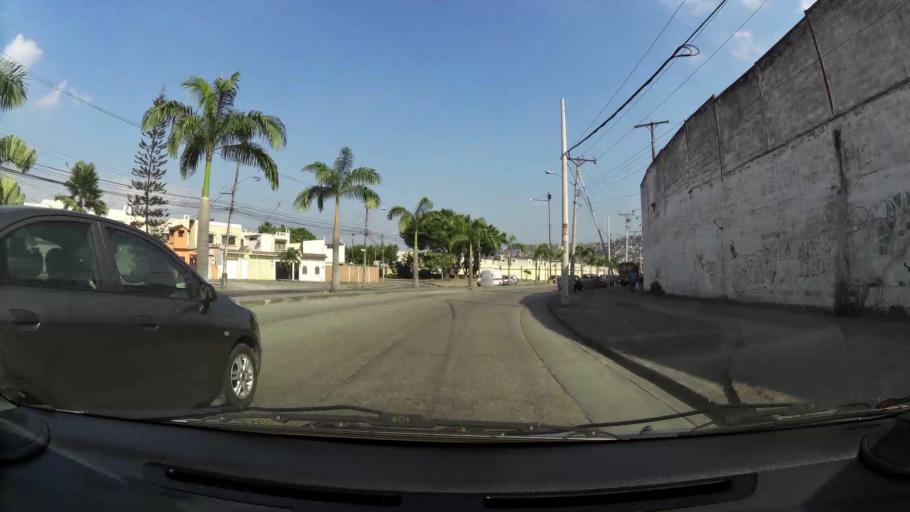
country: EC
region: Guayas
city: Guayaquil
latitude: -2.1350
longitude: -79.9282
